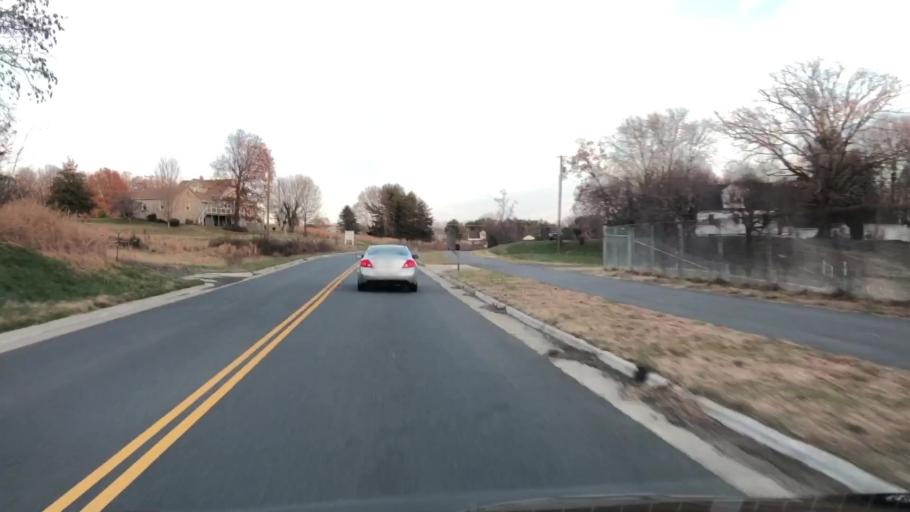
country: US
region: Virginia
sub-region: Stafford County
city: Falmouth
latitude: 38.3709
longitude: -77.4941
